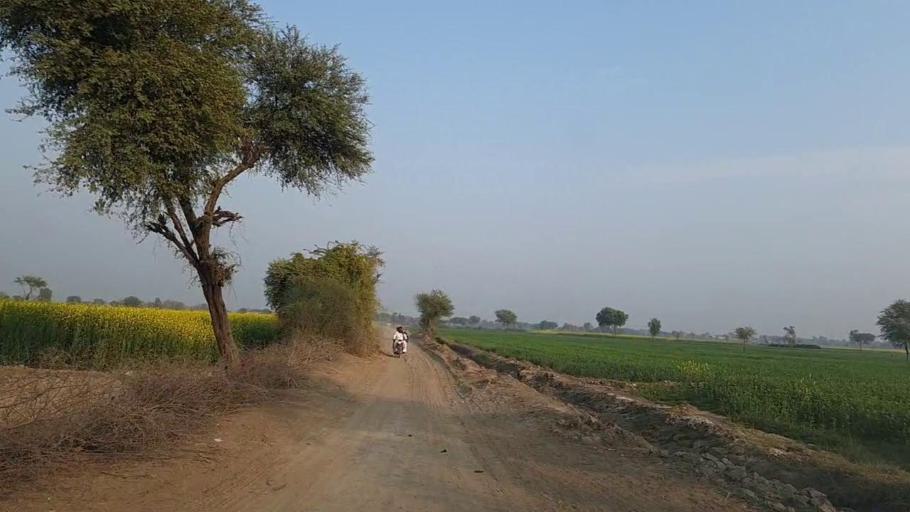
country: PK
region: Sindh
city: Jam Sahib
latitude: 26.3205
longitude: 68.5905
